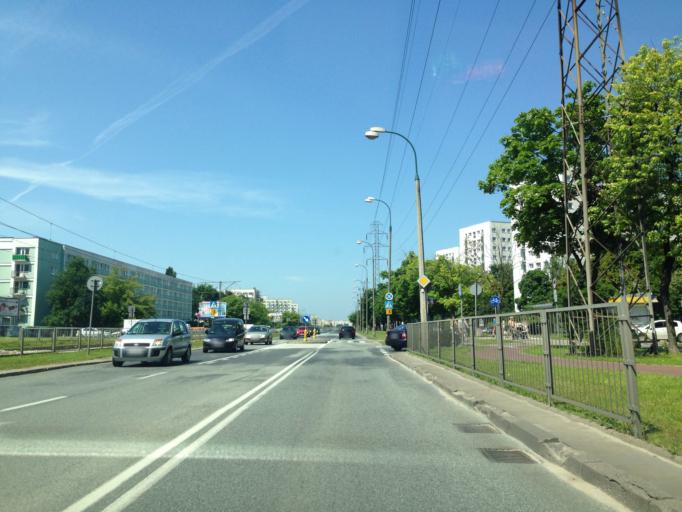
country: PL
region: Masovian Voivodeship
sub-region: Warszawa
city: Zoliborz
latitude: 52.2651
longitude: 20.9695
